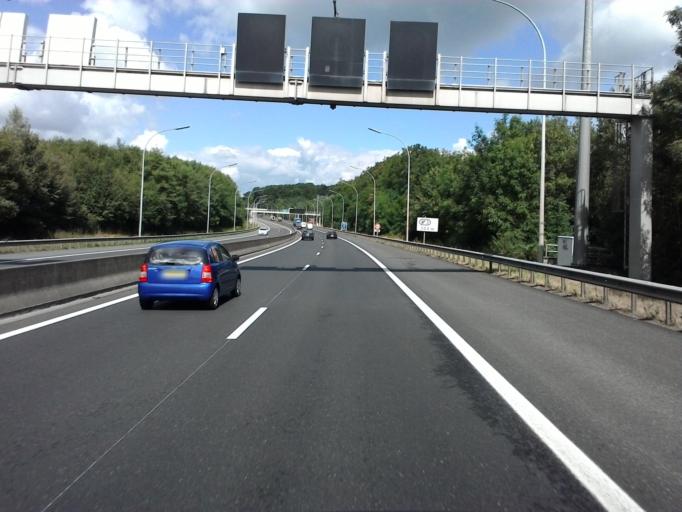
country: LU
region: Luxembourg
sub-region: Canton de Luxembourg
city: Strassen
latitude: 49.6256
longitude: 6.0793
